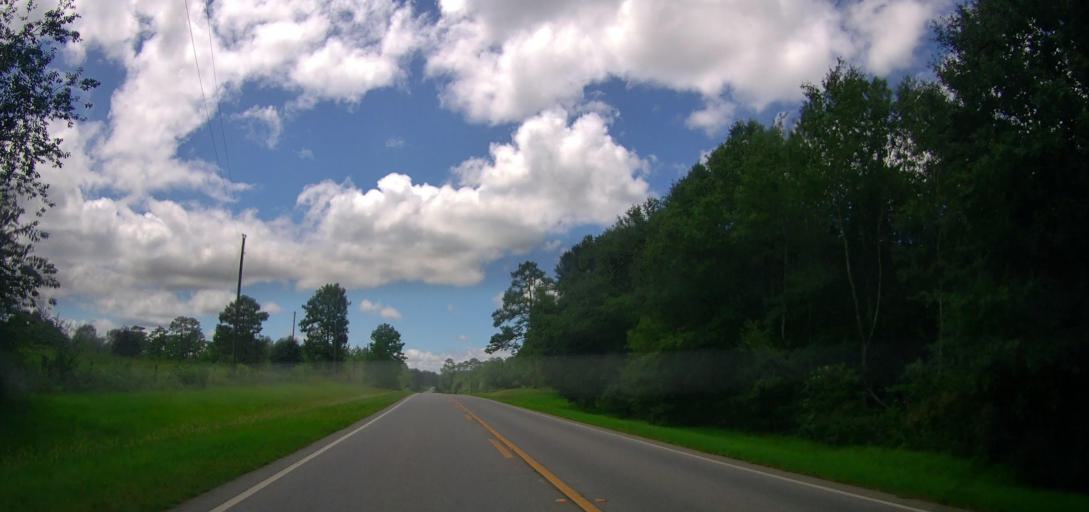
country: US
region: Georgia
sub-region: Turner County
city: Ashburn
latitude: 31.7224
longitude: -83.5699
